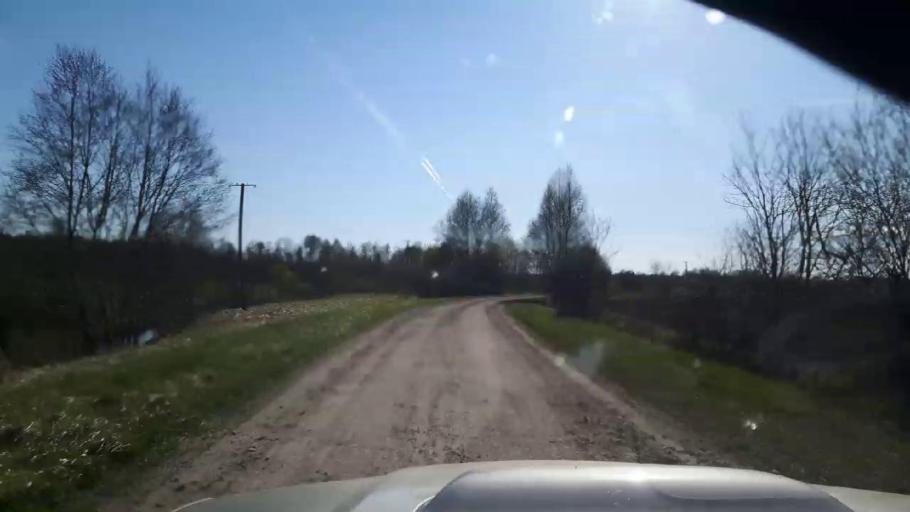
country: EE
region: Paernumaa
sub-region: Tootsi vald
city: Tootsi
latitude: 58.4135
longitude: 24.8503
